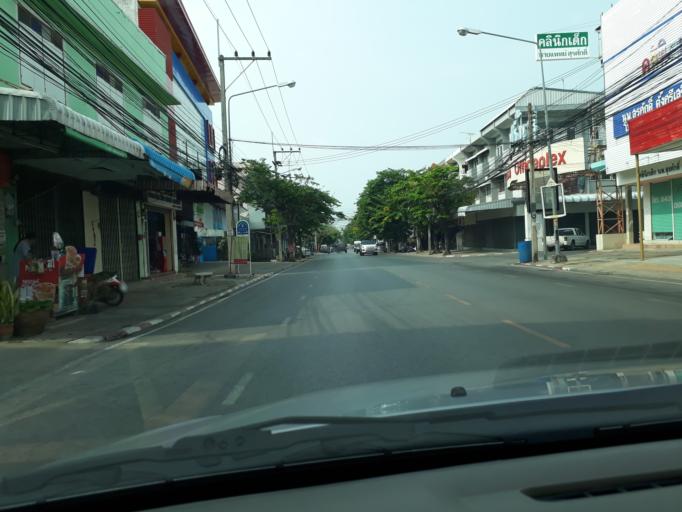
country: TH
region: Khon Kaen
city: Khon Kaen
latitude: 16.4377
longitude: 102.8347
